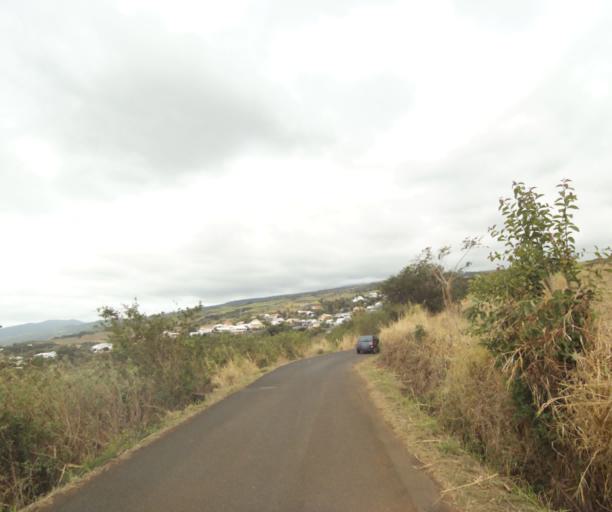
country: RE
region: Reunion
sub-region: Reunion
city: Saint-Paul
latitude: -21.0263
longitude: 55.3019
